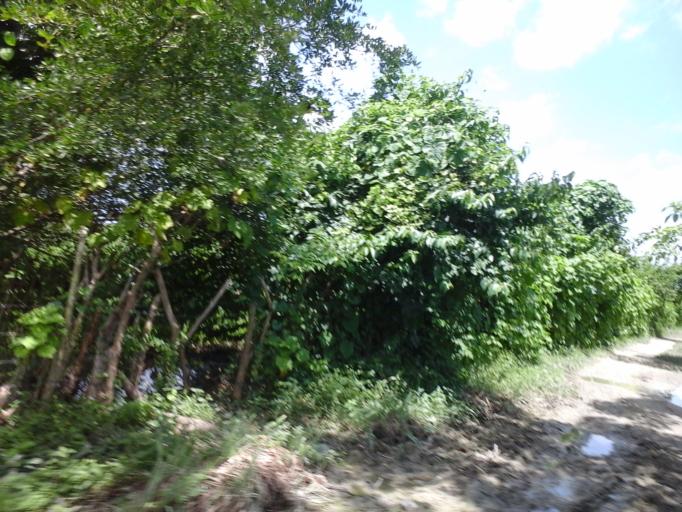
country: CO
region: Bolivar
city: San Pablo
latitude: 10.1550
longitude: -75.2738
